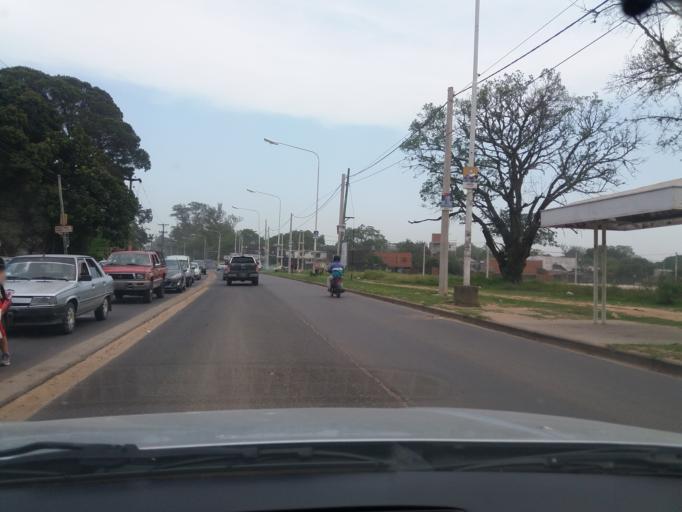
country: AR
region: Corrientes
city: Corrientes
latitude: -27.5075
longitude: -58.8106
